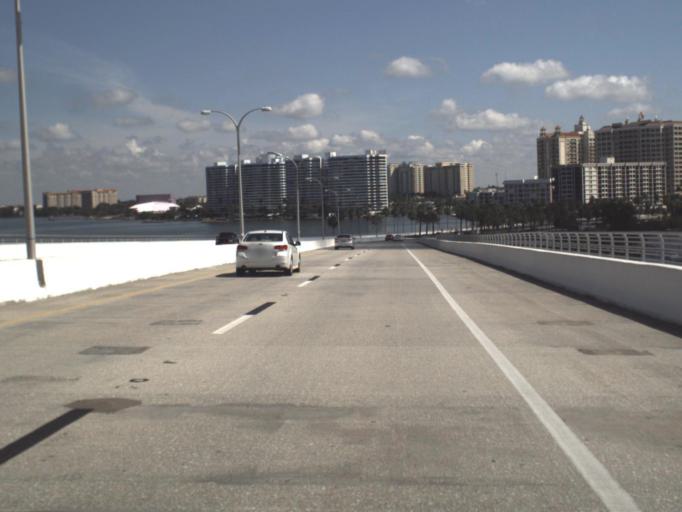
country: US
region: Florida
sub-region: Sarasota County
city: Sarasota
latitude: 27.3327
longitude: -82.5556
